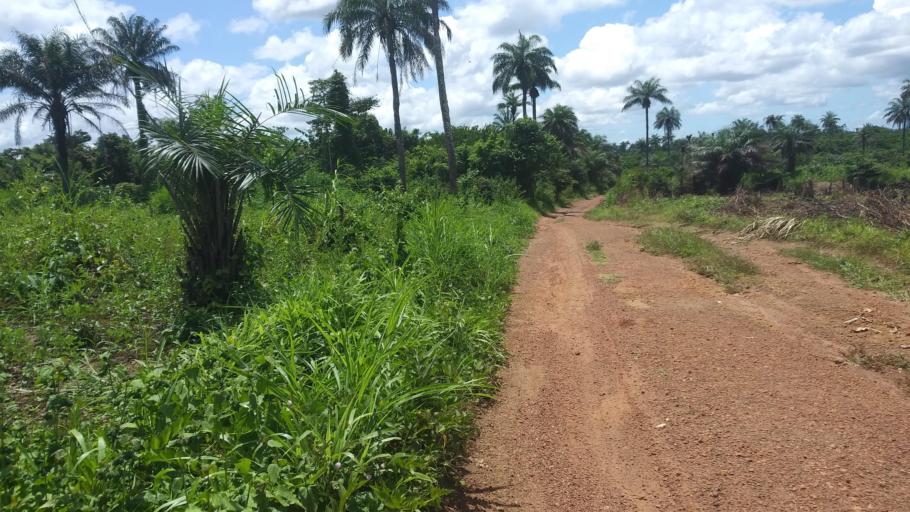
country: SL
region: Northern Province
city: Binkolo
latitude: 8.8795
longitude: -11.9621
